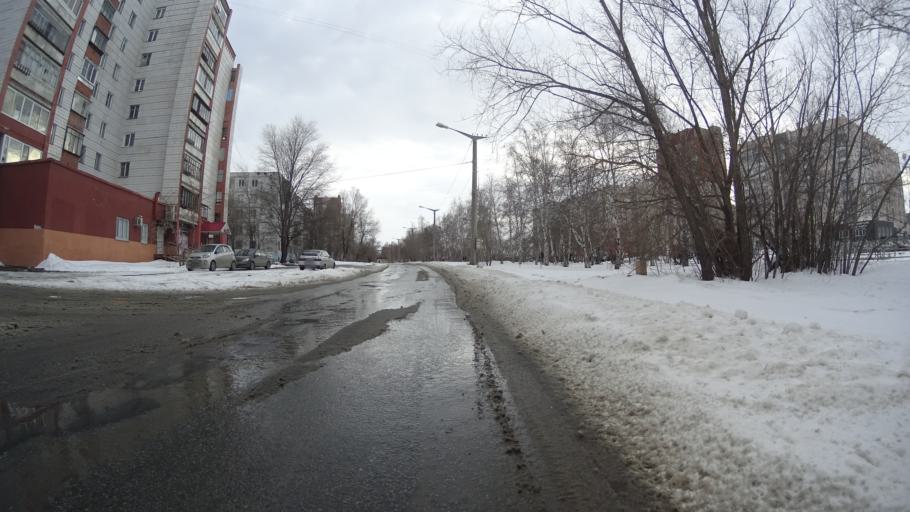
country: RU
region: Chelyabinsk
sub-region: Gorod Chelyabinsk
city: Chelyabinsk
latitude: 55.1979
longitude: 61.3225
